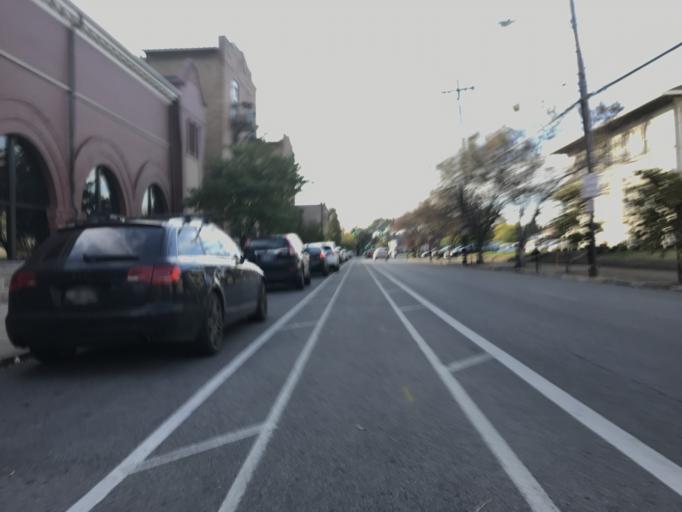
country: US
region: Kentucky
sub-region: Jefferson County
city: Louisville
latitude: 38.2419
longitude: -85.7594
